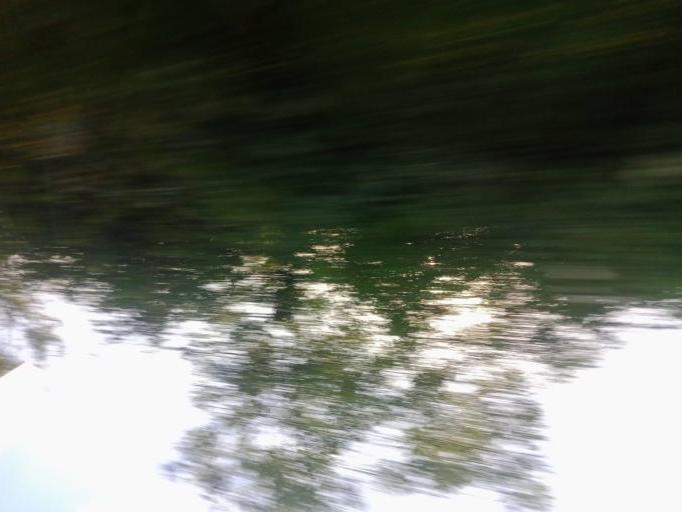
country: IE
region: Leinster
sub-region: Kilkenny
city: Kilkenny
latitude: 52.7245
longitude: -7.2371
